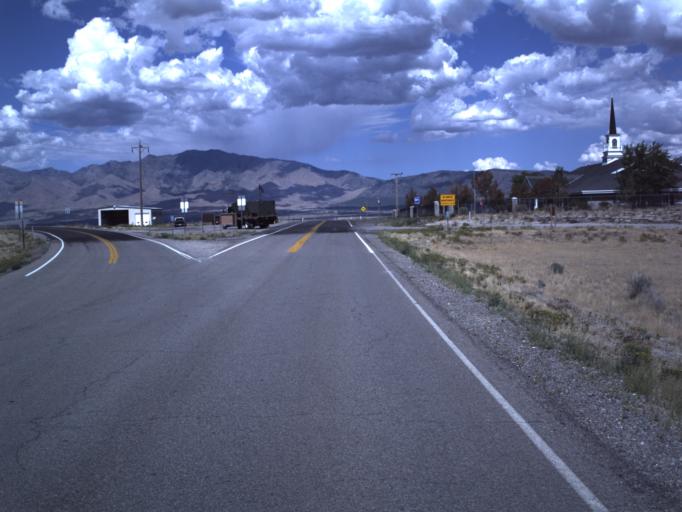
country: US
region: Utah
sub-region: Tooele County
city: Grantsville
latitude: 40.2313
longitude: -112.7241
